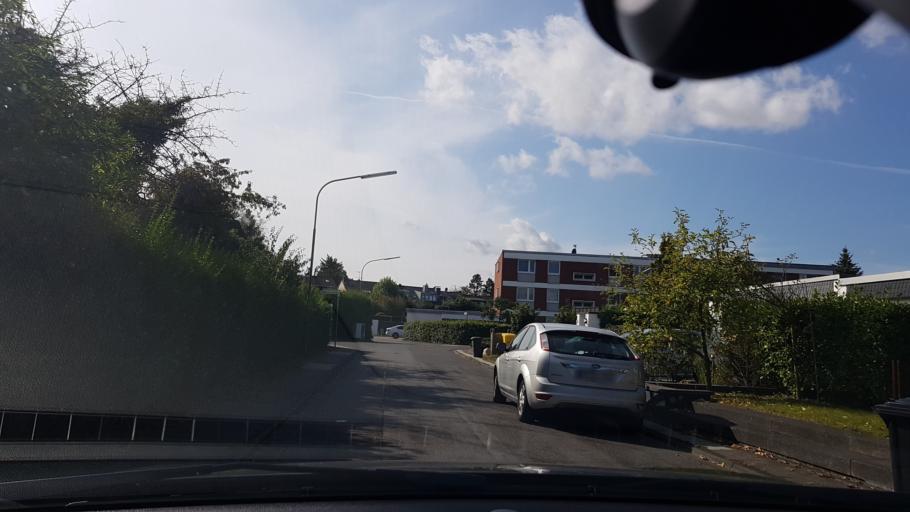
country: DE
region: North Rhine-Westphalia
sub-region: Regierungsbezirk Dusseldorf
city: Neuss
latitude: 51.1412
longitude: 6.6989
